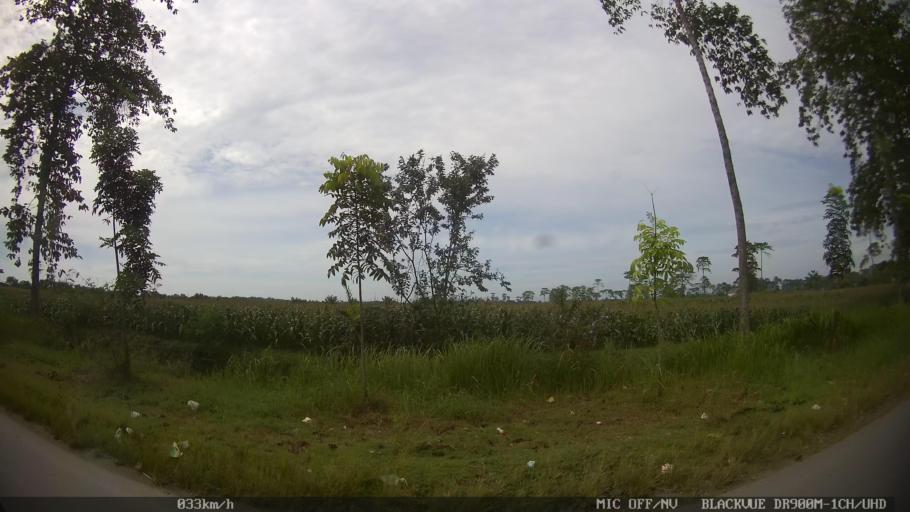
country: ID
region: North Sumatra
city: Percut
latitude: 3.6201
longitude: 98.7704
